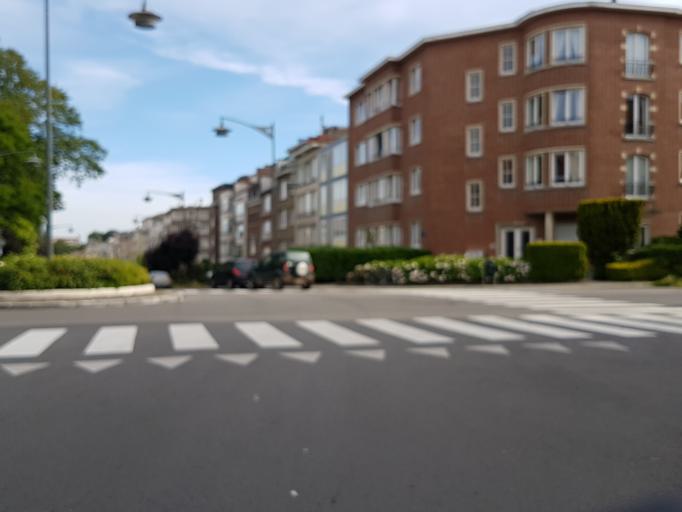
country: BE
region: Brussels Capital
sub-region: Bruxelles-Capitale
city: Brussels
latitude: 50.8110
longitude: 4.3878
